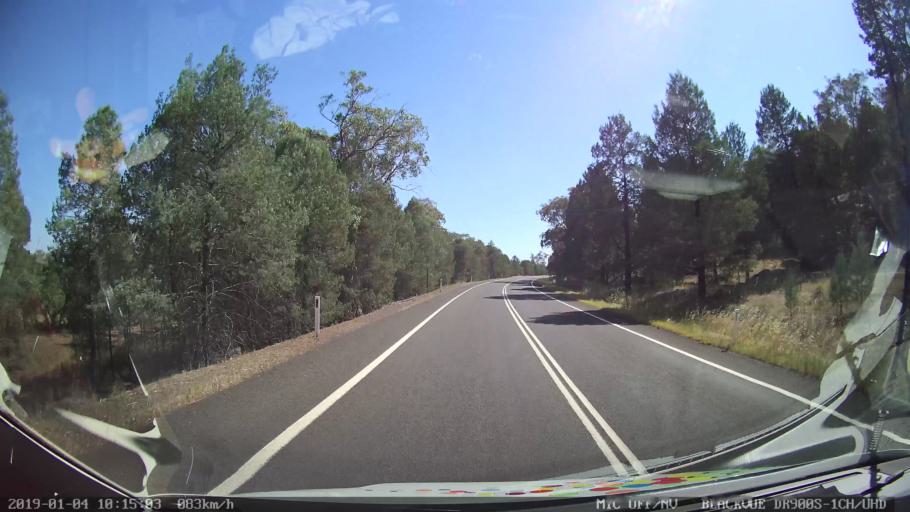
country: AU
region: New South Wales
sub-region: Cabonne
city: Canowindra
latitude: -33.3901
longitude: 148.4170
